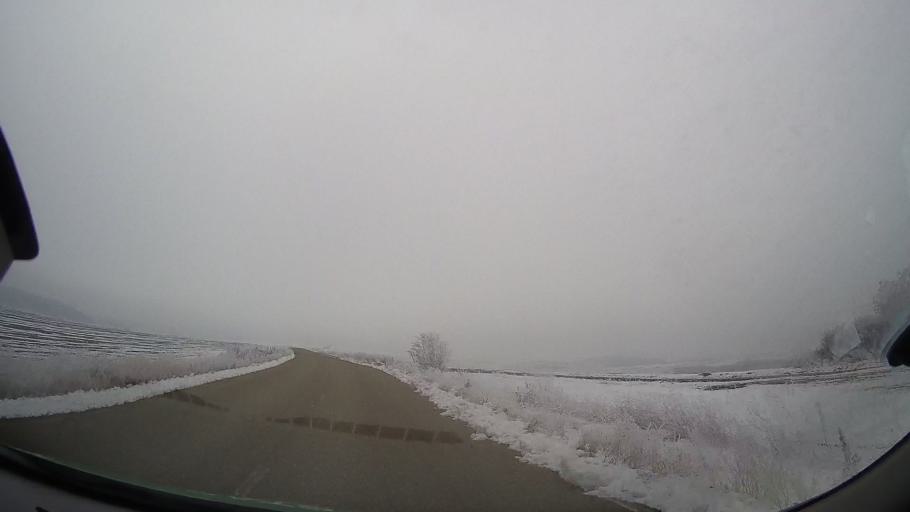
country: RO
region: Vaslui
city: Coroiesti
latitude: 46.2319
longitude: 27.4776
